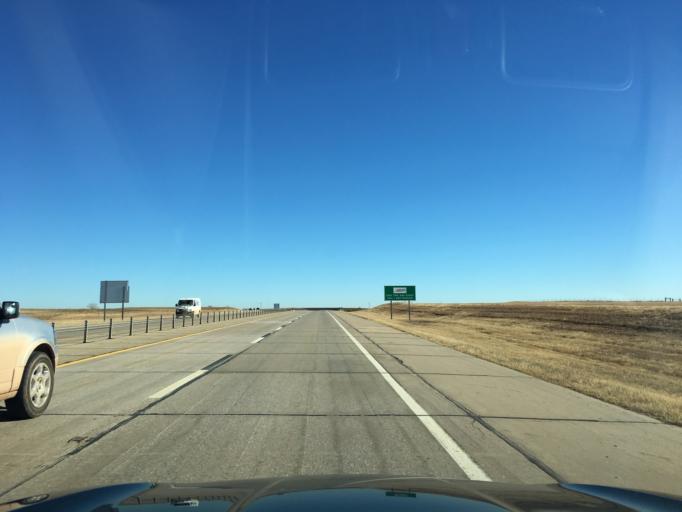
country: US
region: Oklahoma
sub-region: Noble County
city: Perry
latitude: 36.3997
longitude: -97.3077
